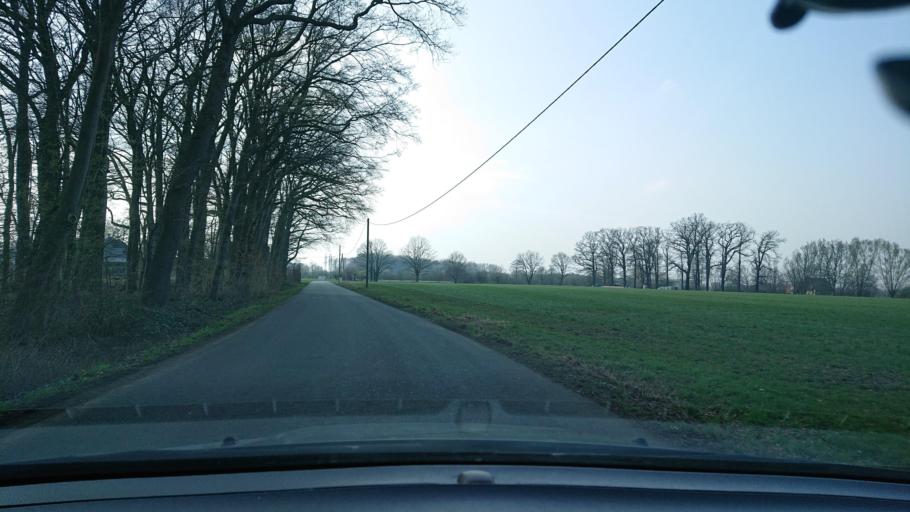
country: DE
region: North Rhine-Westphalia
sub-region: Regierungsbezirk Detmold
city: Langenberg
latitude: 51.7571
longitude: 8.3772
